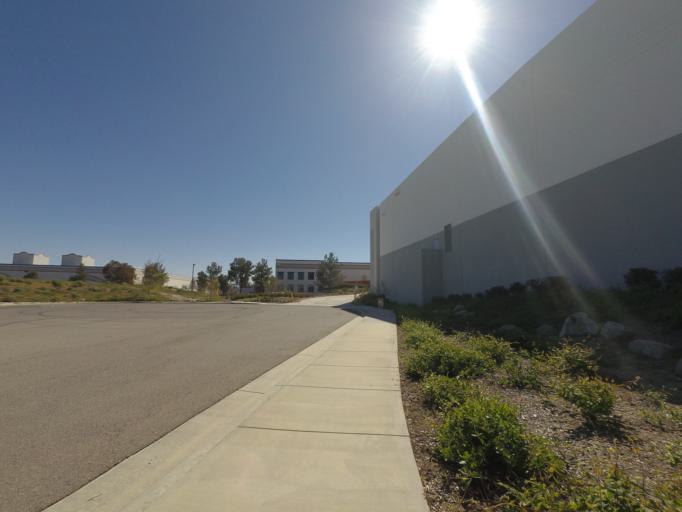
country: US
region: California
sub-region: Riverside County
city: March Air Force Base
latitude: 33.9189
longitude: -117.2949
